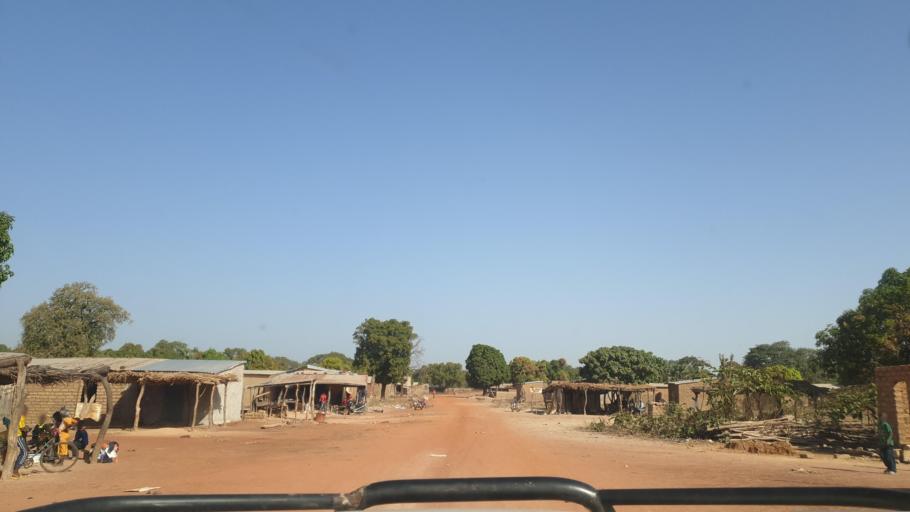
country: ML
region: Sikasso
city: Kolondieba
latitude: 11.7675
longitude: -6.9023
